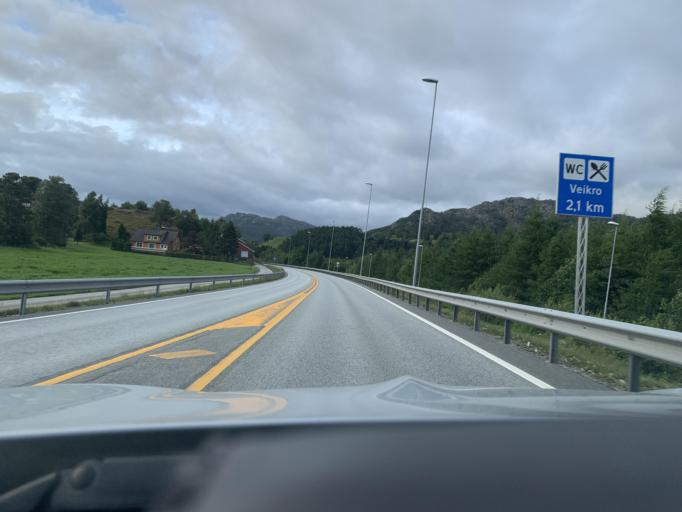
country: NO
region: Rogaland
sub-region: Bjerkreim
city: Vikesa
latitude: 58.6119
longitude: 6.0922
